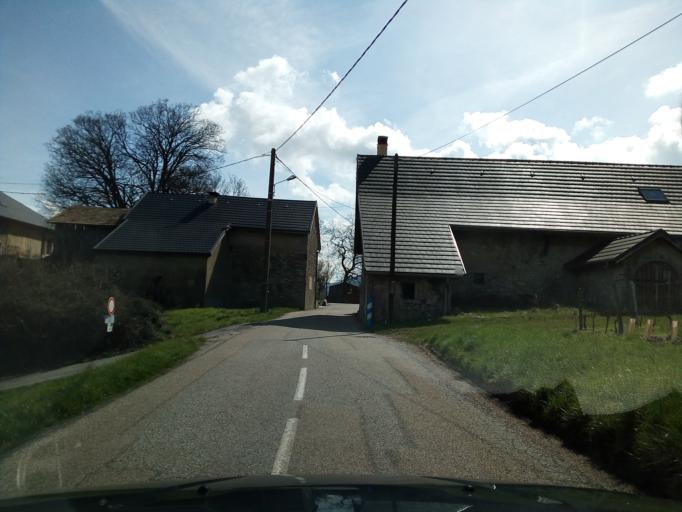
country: FR
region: Rhone-Alpes
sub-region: Departement de la Savoie
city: Saint-Baldoph
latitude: 45.5358
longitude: 5.9473
